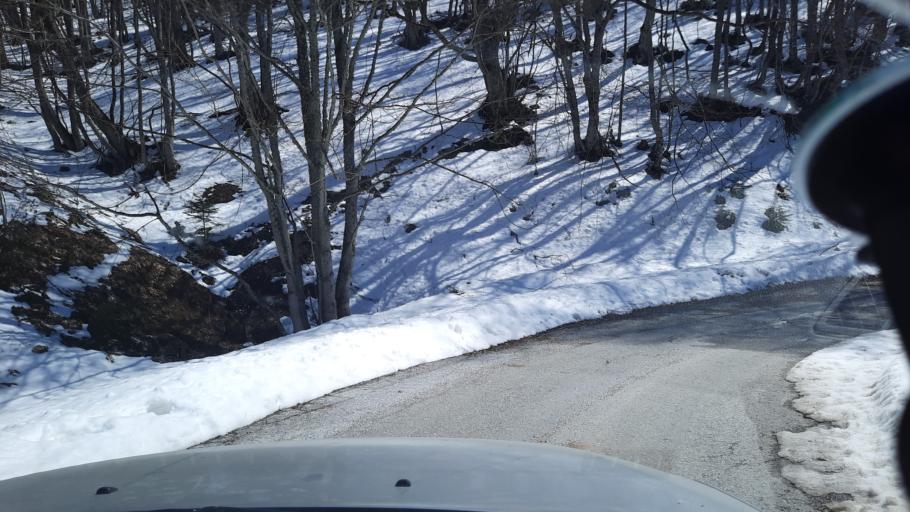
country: MK
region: Gostivar
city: Vrutok
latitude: 41.7088
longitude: 20.7387
